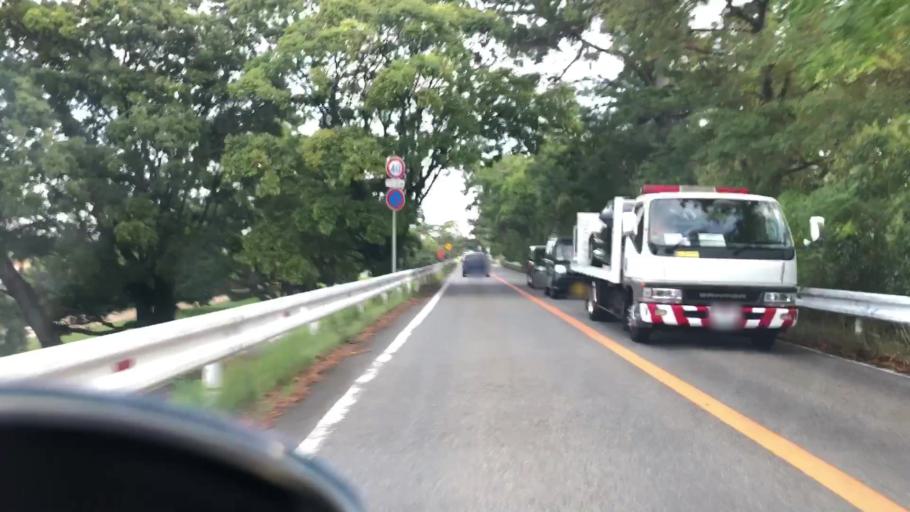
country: JP
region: Hyogo
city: Itami
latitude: 34.7614
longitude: 135.3720
